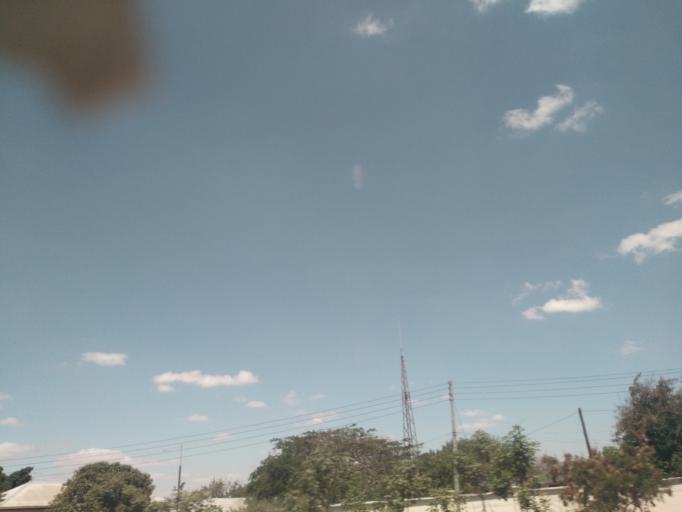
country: TZ
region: Dodoma
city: Dodoma
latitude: -6.1810
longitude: 35.7331
